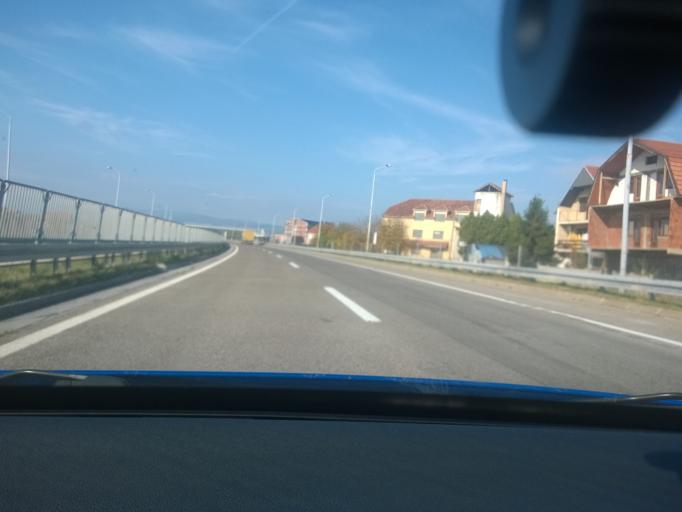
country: RS
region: Central Serbia
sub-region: Nisavski Okrug
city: Nis
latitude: 43.3461
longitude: 21.8767
